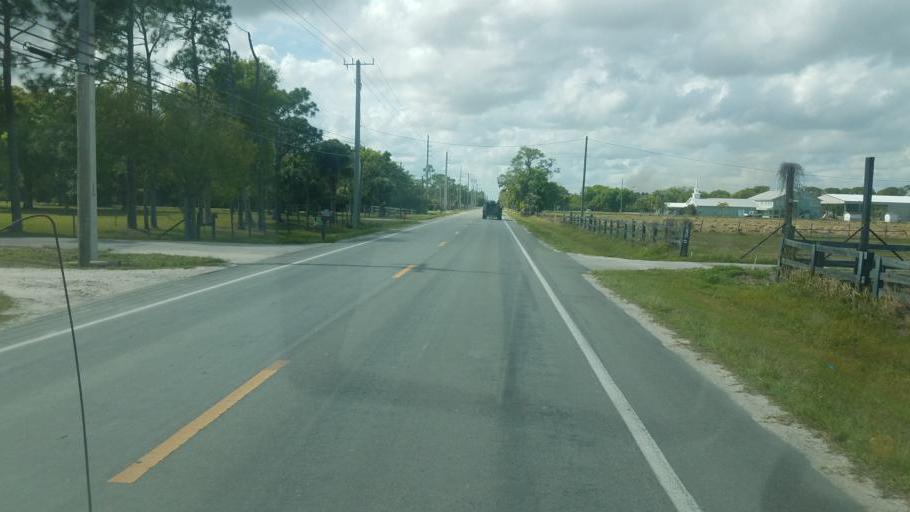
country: US
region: Florida
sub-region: Saint Lucie County
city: Lakewood Park
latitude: 27.4477
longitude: -80.4520
